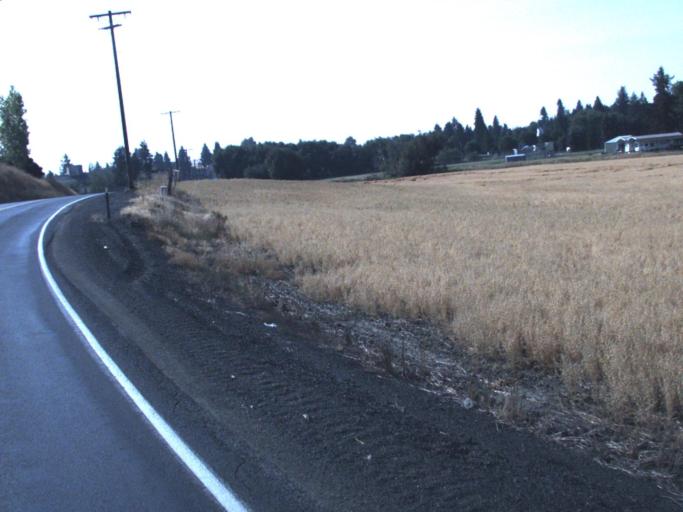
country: US
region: Washington
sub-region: Whitman County
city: Colfax
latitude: 47.1347
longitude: -117.2428
